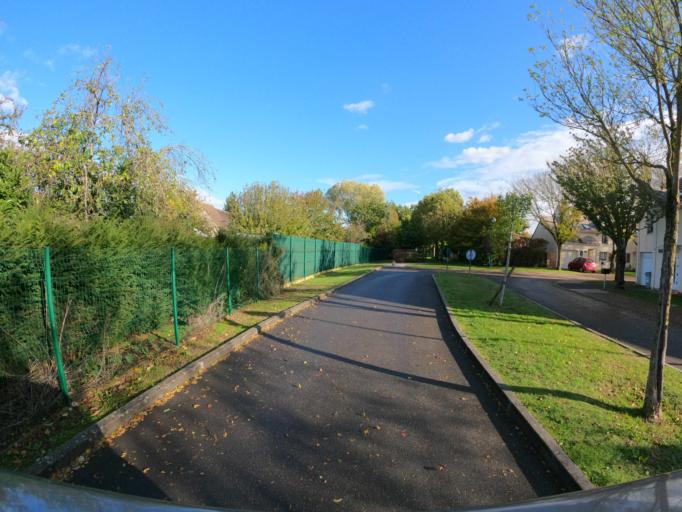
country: FR
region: Ile-de-France
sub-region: Departement de Seine-et-Marne
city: Bailly-Romainvilliers
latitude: 48.8487
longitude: 2.8235
